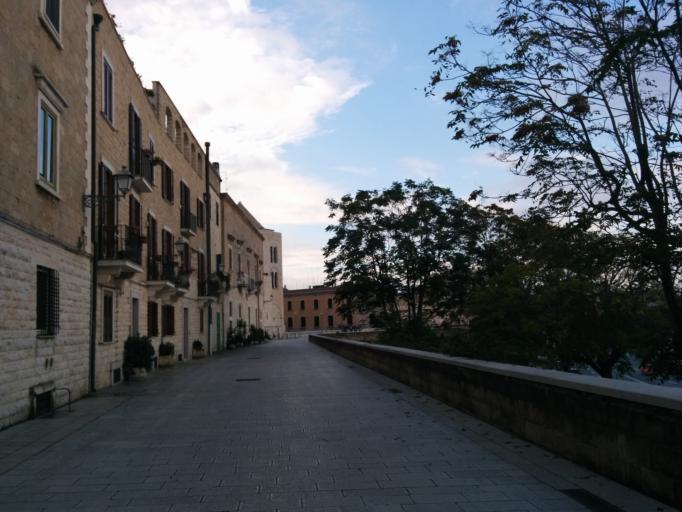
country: IT
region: Apulia
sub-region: Provincia di Bari
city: Bari
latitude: 41.1296
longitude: 16.8714
